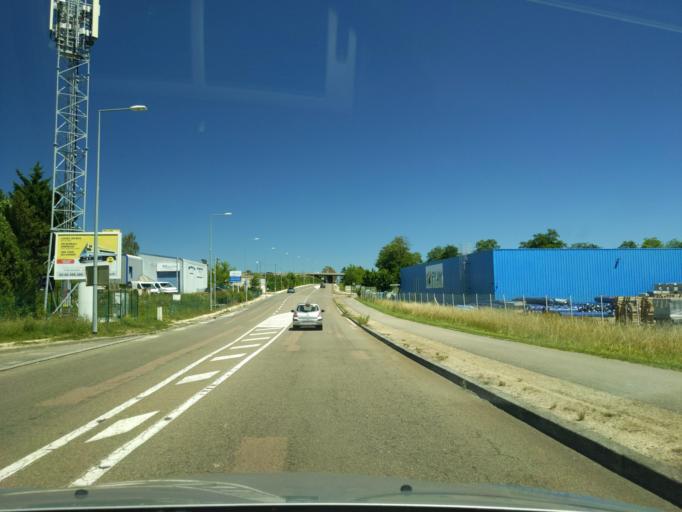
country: FR
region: Bourgogne
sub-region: Departement de la Cote-d'Or
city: Ruffey-les-Echirey
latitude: 47.3547
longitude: 5.0634
